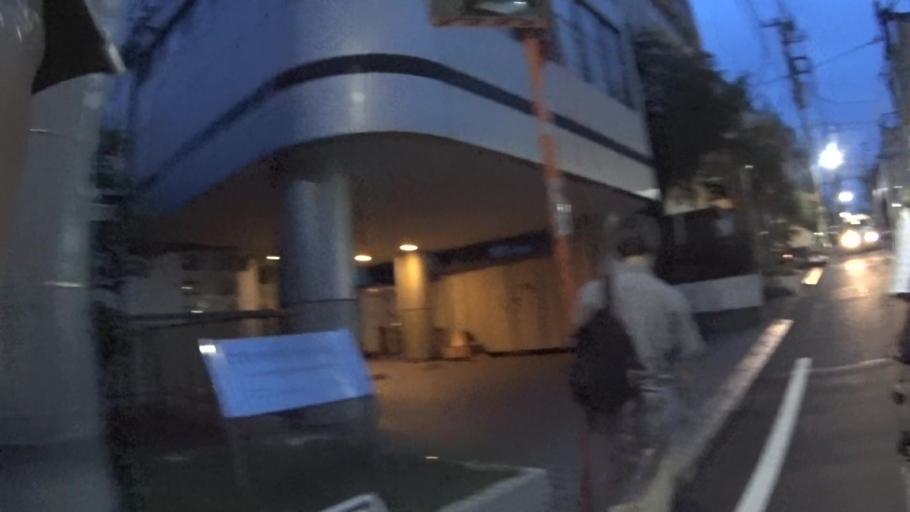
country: JP
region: Tokyo
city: Tokyo
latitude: 35.7029
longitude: 139.7361
